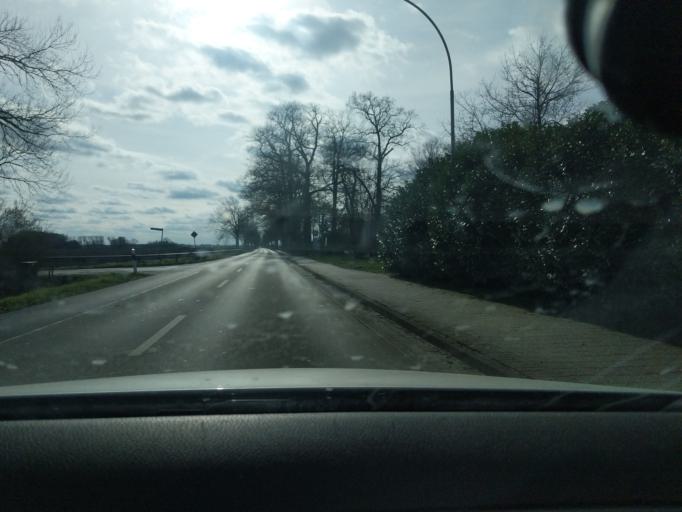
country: DE
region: Lower Saxony
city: Drochtersen
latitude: 53.6946
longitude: 9.4073
